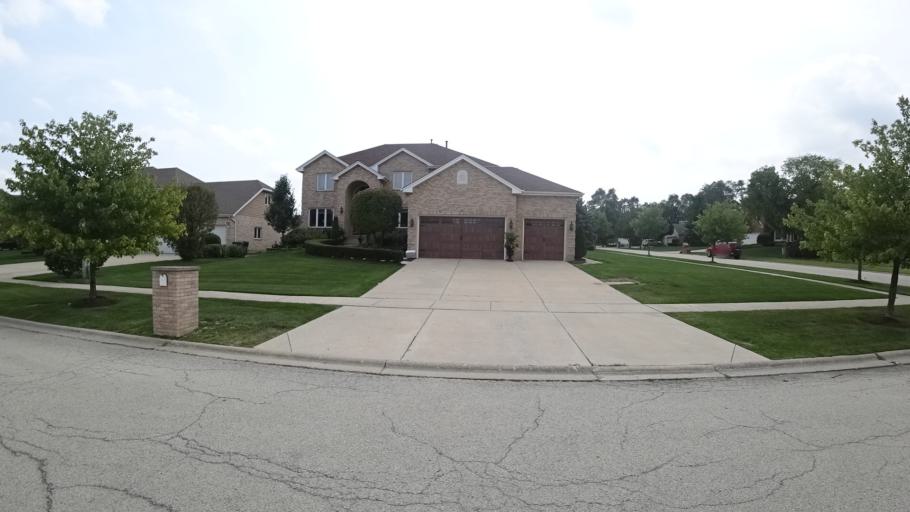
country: US
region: Illinois
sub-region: Will County
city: Goodings Grove
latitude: 41.6253
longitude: -87.9129
